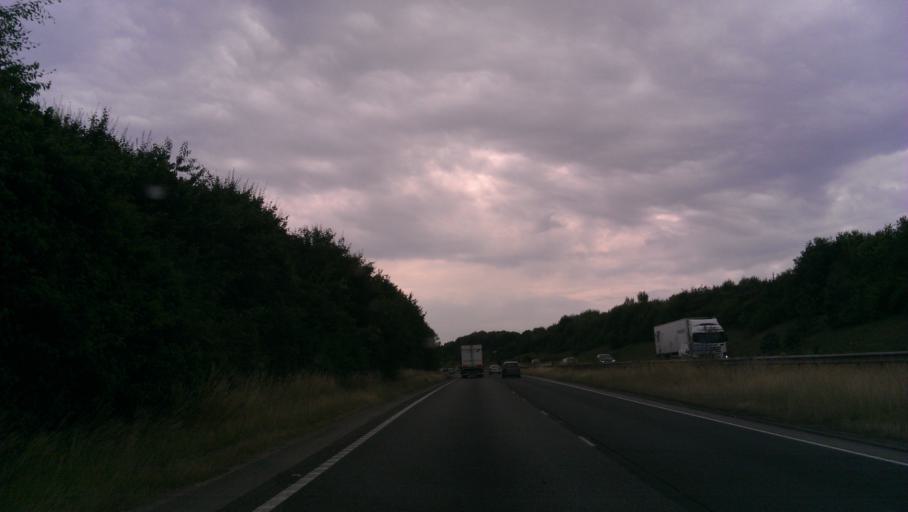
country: GB
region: England
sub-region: Kent
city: Newington
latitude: 51.3358
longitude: 0.6702
